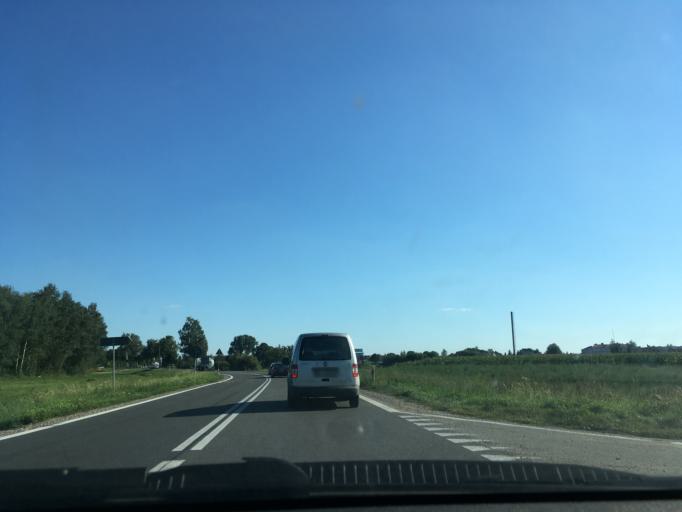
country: PL
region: Podlasie
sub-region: Powiat sokolski
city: Suchowola
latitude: 53.4526
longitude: 23.0873
